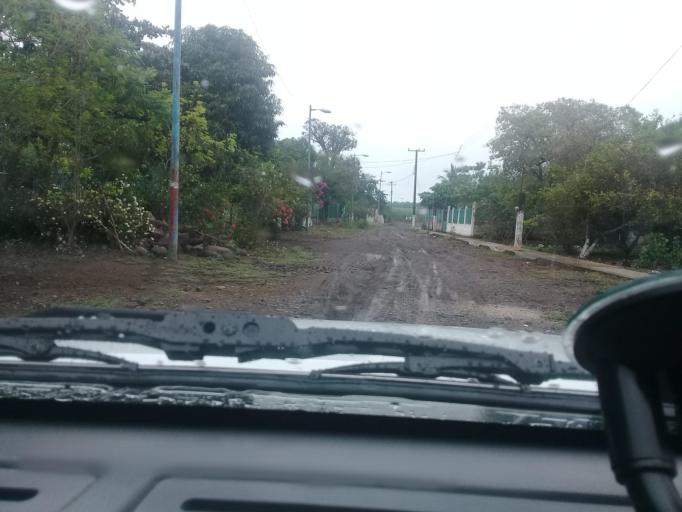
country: MX
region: Veracruz
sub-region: Puente Nacional
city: Cabezas
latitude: 19.3576
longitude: -96.3785
